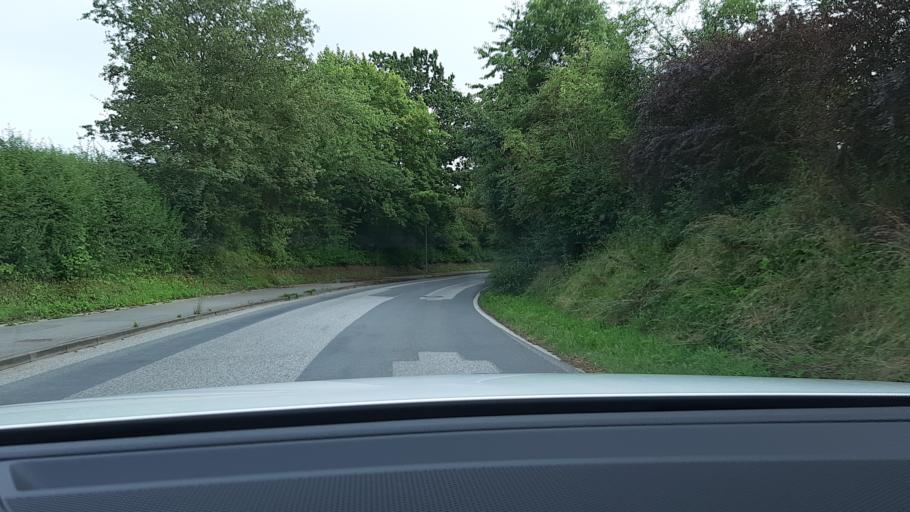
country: DE
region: Schleswig-Holstein
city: Wesenberg
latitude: 53.8382
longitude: 10.5558
